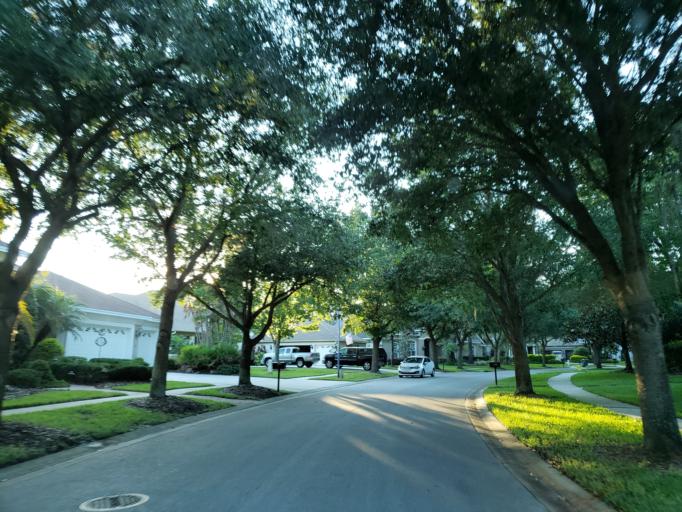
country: US
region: Florida
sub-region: Hillsborough County
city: Boyette
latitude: 27.8348
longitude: -82.2223
